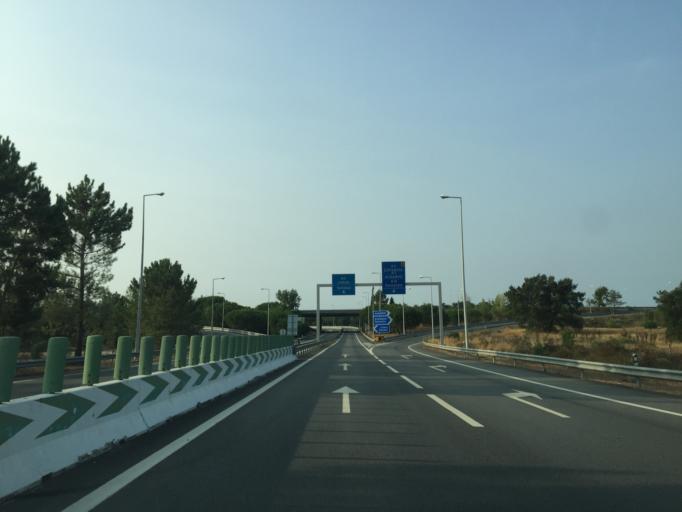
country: PT
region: Setubal
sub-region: Setubal
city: Setubal
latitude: 38.5991
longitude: -8.6737
